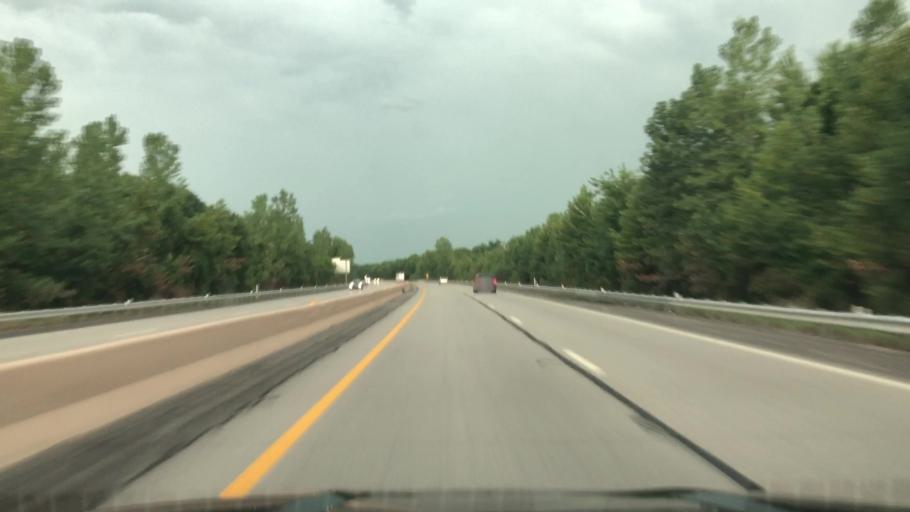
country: US
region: Oklahoma
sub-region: Rogers County
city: Claremore
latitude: 36.2929
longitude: -95.6089
